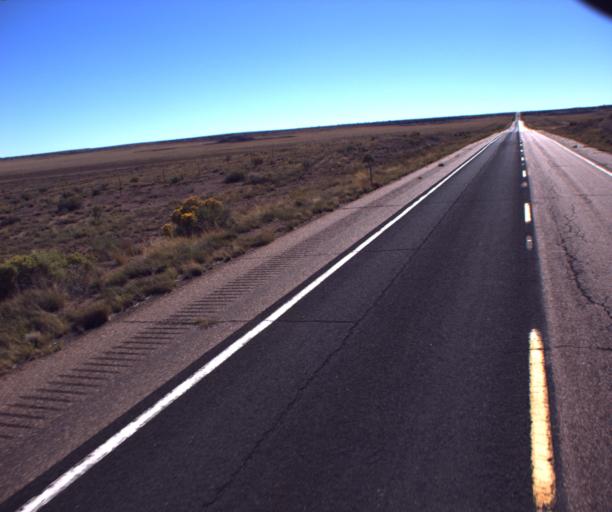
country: US
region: Arizona
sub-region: Navajo County
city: Snowflake
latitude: 34.7341
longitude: -109.7857
